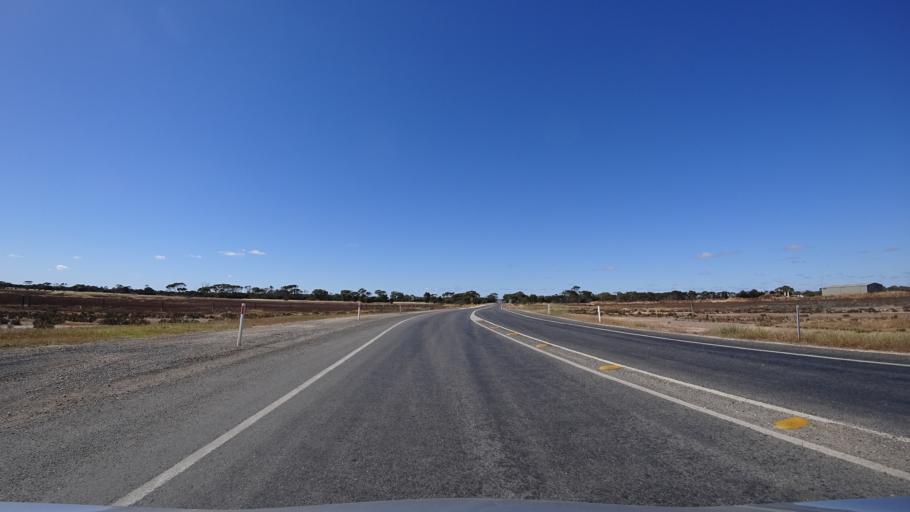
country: AU
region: South Australia
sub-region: Kangaroo Island
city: Kingscote
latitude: -35.6785
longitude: 137.5734
